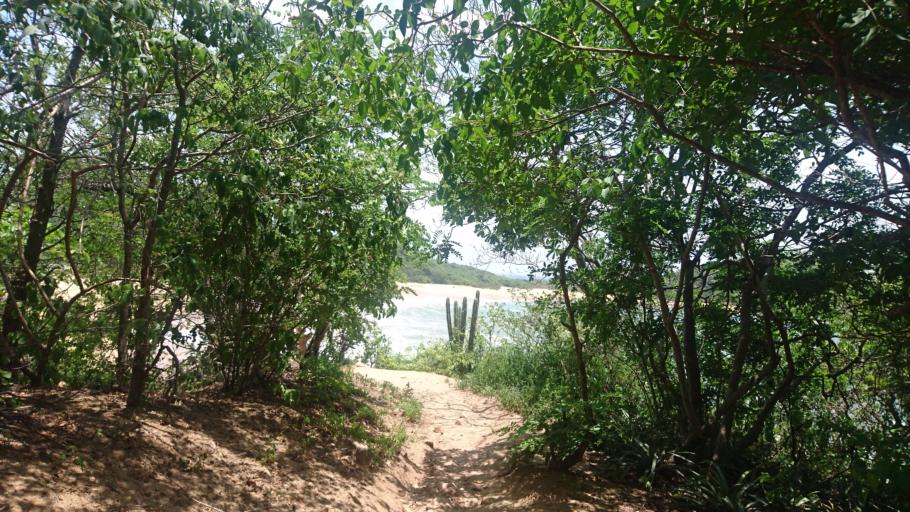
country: MX
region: Oaxaca
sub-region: Santa Maria Huatulco
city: Crucecita
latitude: 15.7808
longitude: -96.0673
